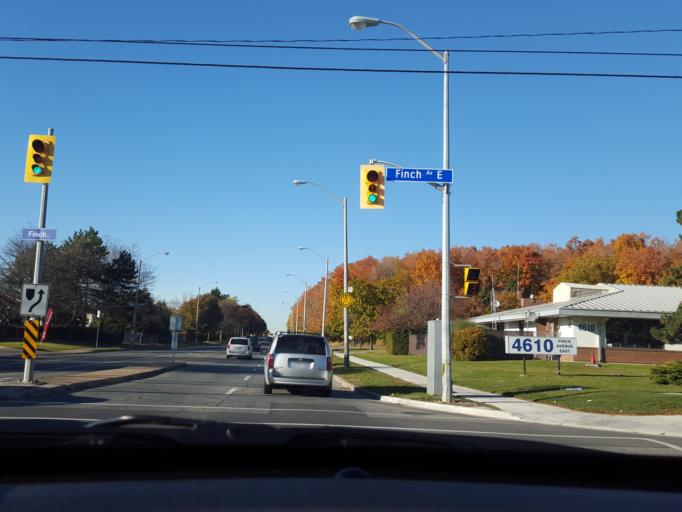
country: CA
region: Ontario
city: Scarborough
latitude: 43.8058
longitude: -79.2773
